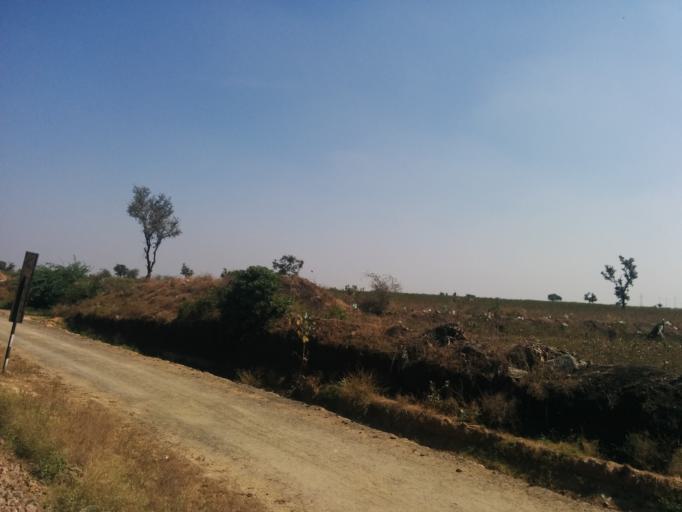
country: IN
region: Karnataka
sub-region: Gadag
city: Gadag
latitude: 15.4383
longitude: 75.6633
